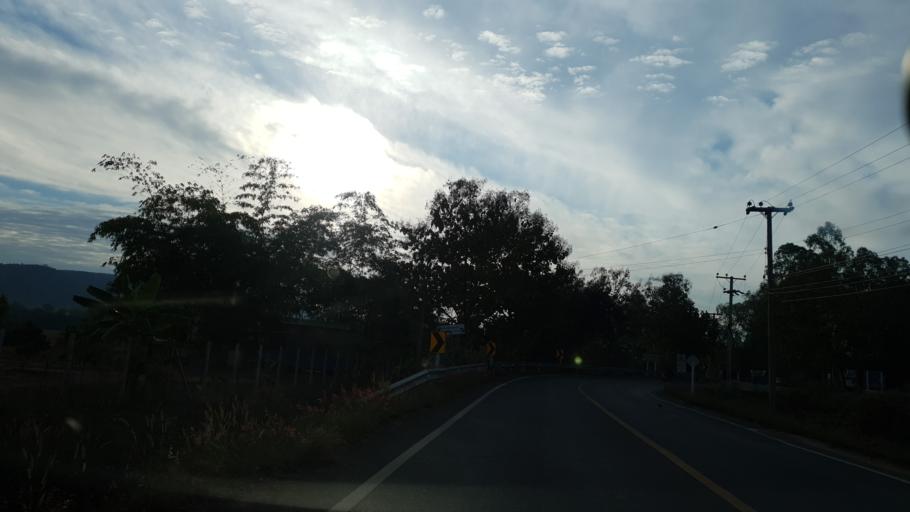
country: TH
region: Lamphun
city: Lamphun
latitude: 18.5153
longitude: 99.0210
